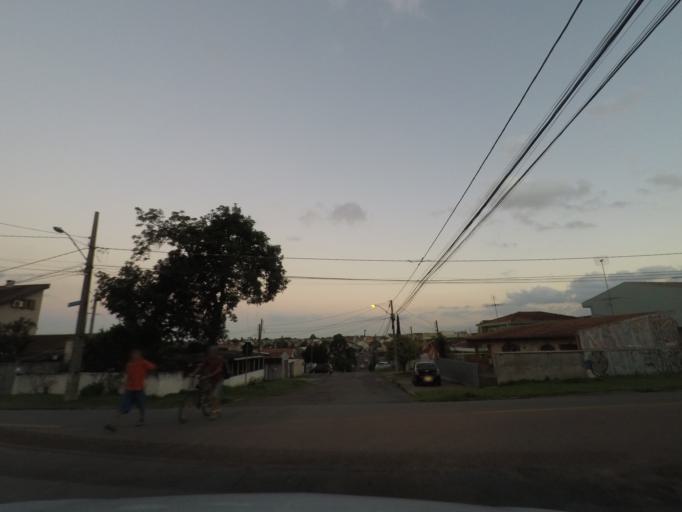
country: BR
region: Parana
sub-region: Sao Jose Dos Pinhais
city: Sao Jose dos Pinhais
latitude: -25.4971
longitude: -49.2644
